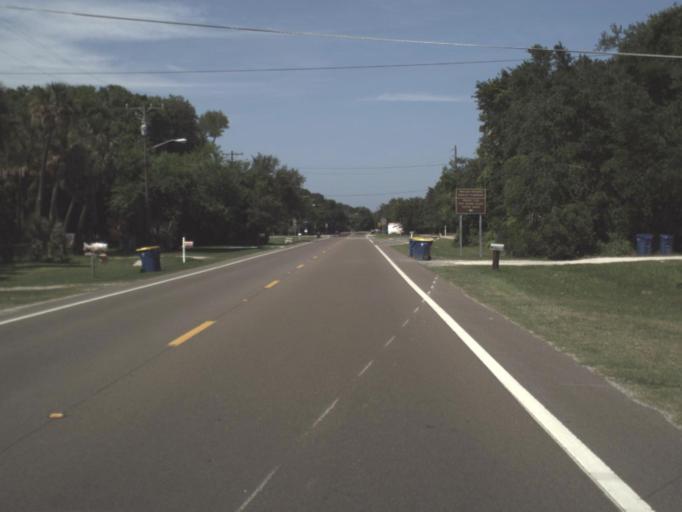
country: US
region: Florida
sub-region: Duval County
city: Atlantic Beach
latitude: 30.4011
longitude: -81.4332
